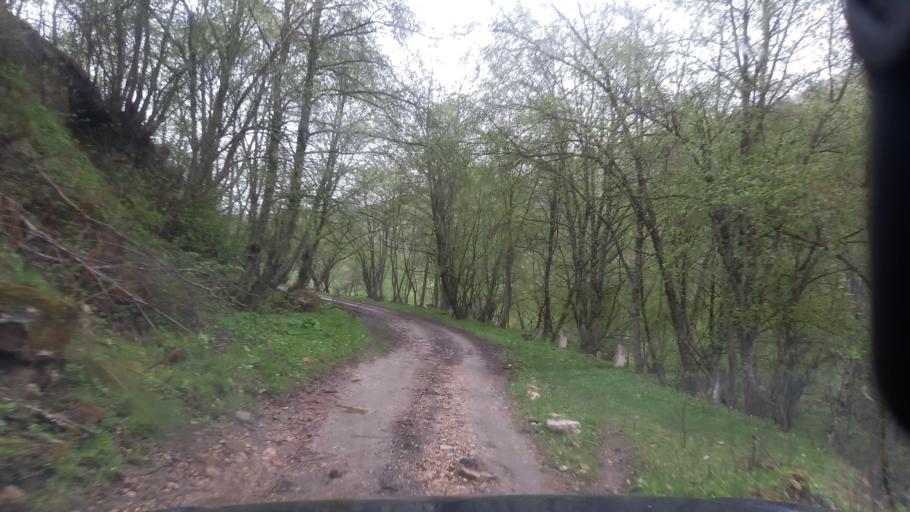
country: RU
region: Kabardino-Balkariya
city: Bylym
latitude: 43.5998
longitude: 42.9205
